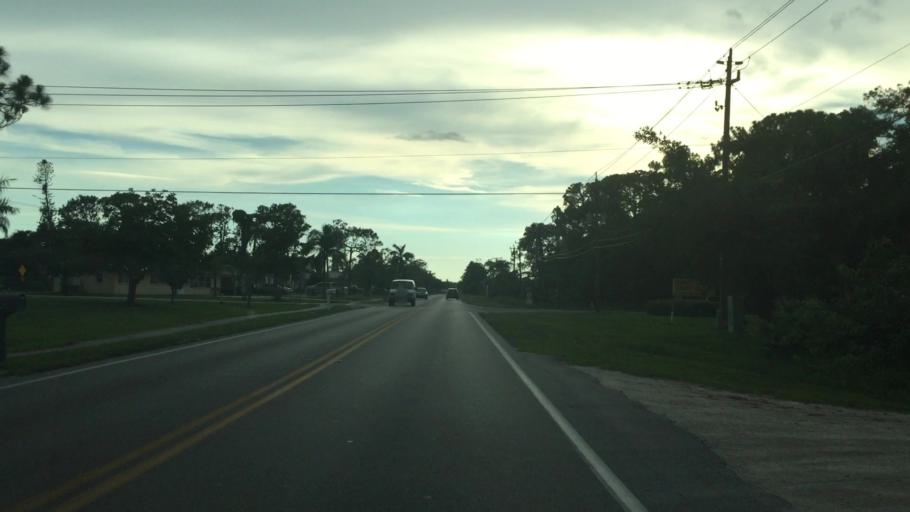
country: US
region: Florida
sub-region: Lee County
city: Villas
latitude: 26.5646
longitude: -81.8590
